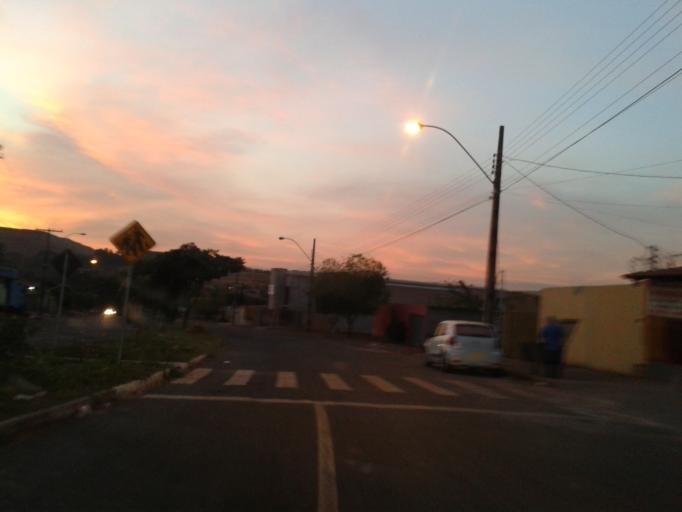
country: BR
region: Goias
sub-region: Goiania
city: Goiania
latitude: -16.6560
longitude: -49.3539
